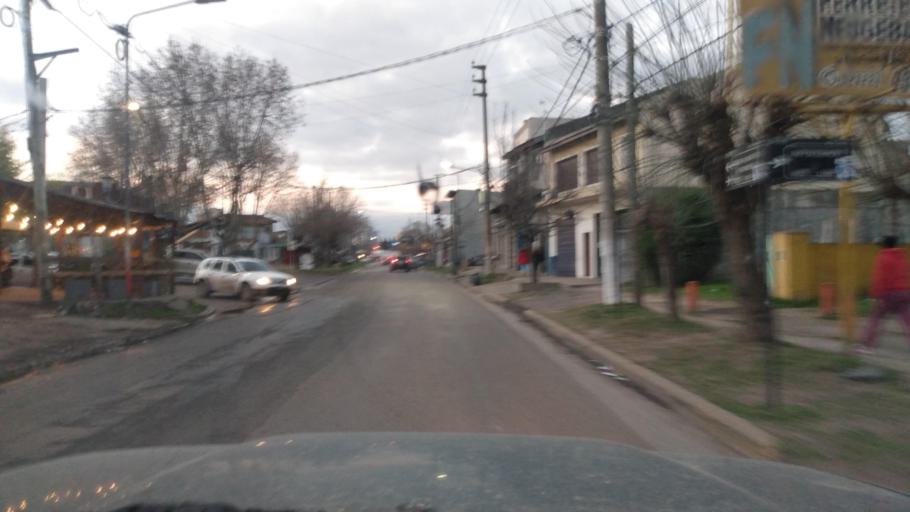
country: AR
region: Buenos Aires
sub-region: Partido de Pilar
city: Pilar
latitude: -34.4654
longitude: -58.9144
